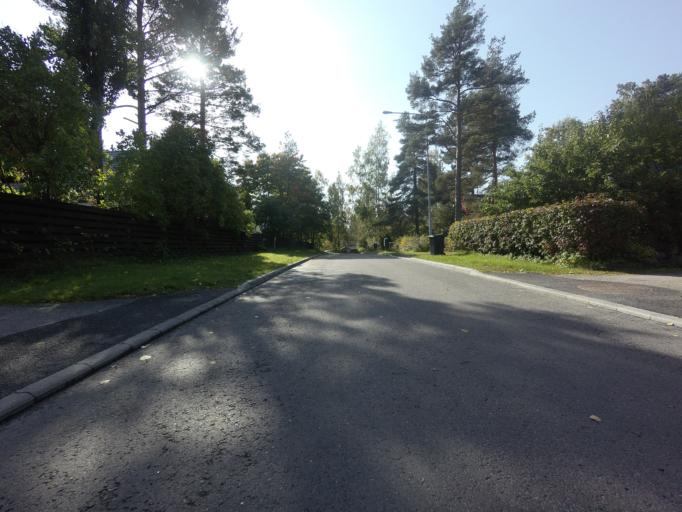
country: FI
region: Uusimaa
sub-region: Helsinki
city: Espoo
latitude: 60.1819
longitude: 24.6544
